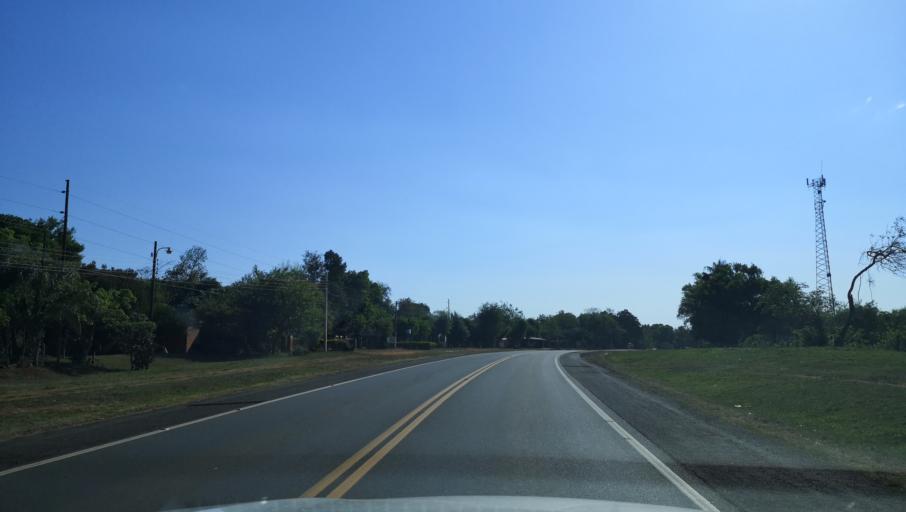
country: PY
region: Misiones
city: Santa Rosa
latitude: -26.8965
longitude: -56.9171
